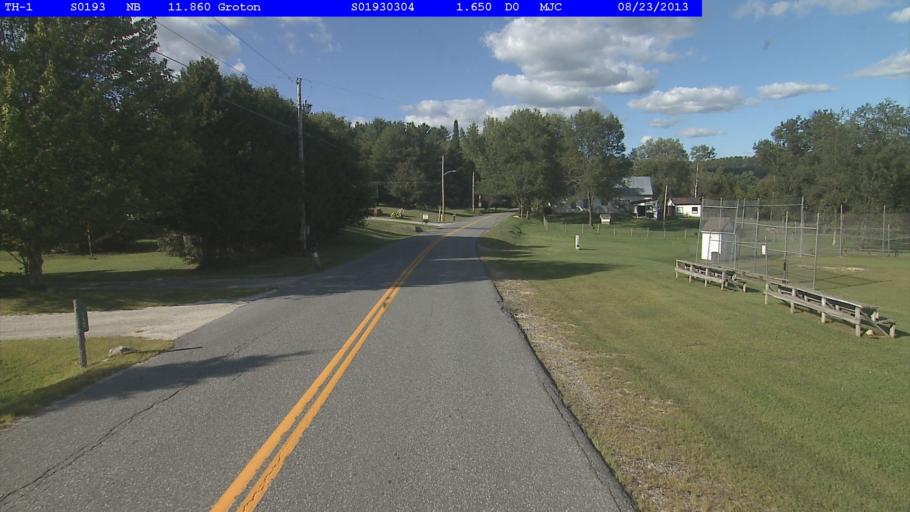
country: US
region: New Hampshire
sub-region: Grafton County
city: Woodsville
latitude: 44.2035
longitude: -72.2002
